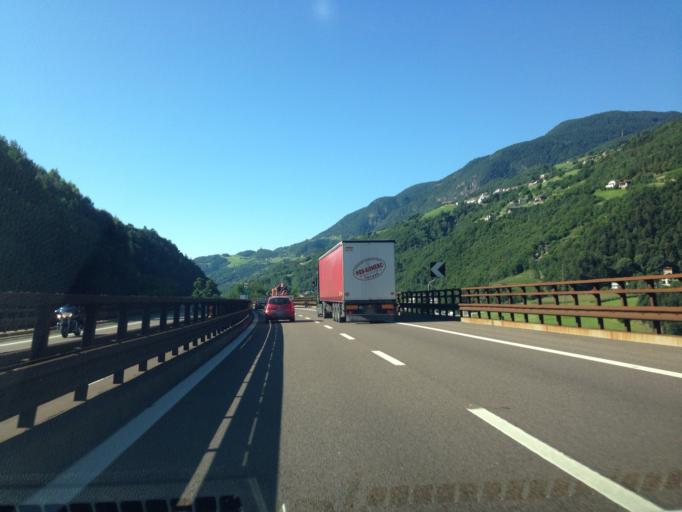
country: IT
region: Trentino-Alto Adige
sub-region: Bolzano
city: Villandro
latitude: 46.6184
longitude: 11.5418
